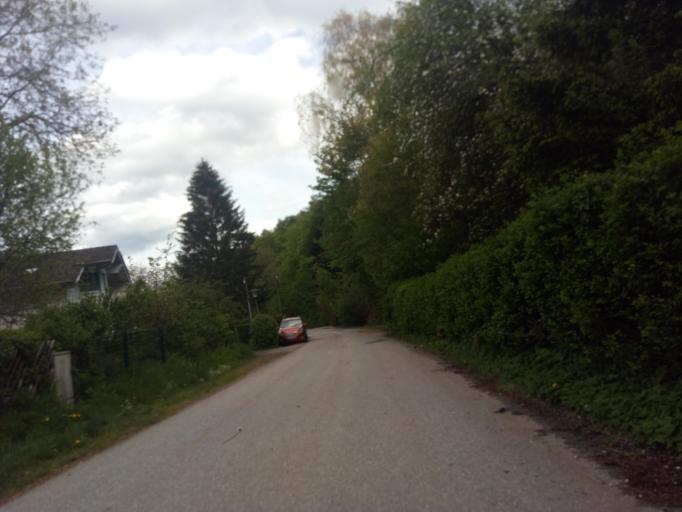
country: AT
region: Lower Austria
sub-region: Politischer Bezirk Wien-Umgebung
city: Wolfsgraben
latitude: 48.1260
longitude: 16.0887
